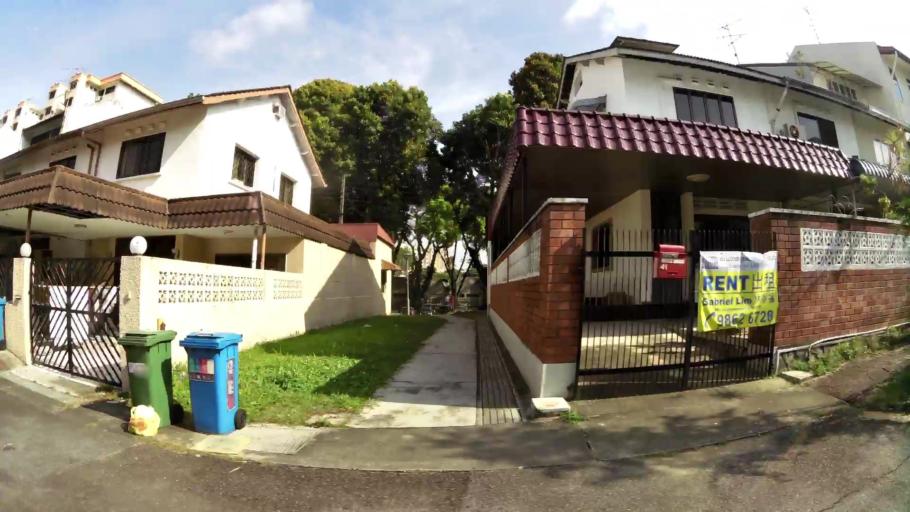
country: SG
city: Singapore
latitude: 1.3543
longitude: 103.8390
